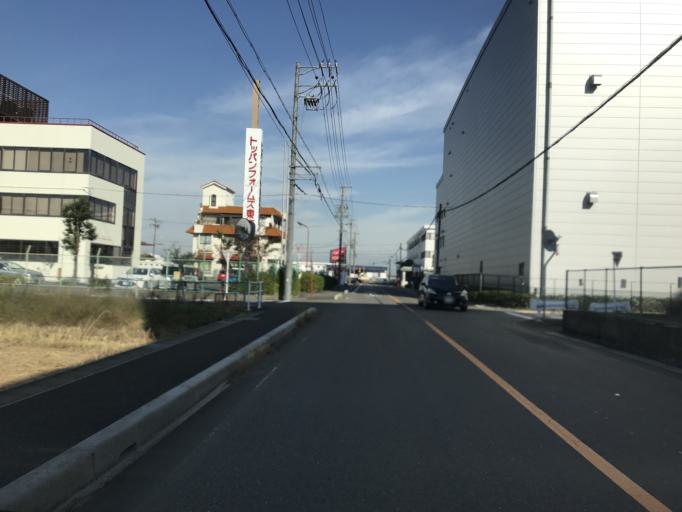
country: JP
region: Aichi
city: Iwakura
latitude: 35.2305
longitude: 136.8528
